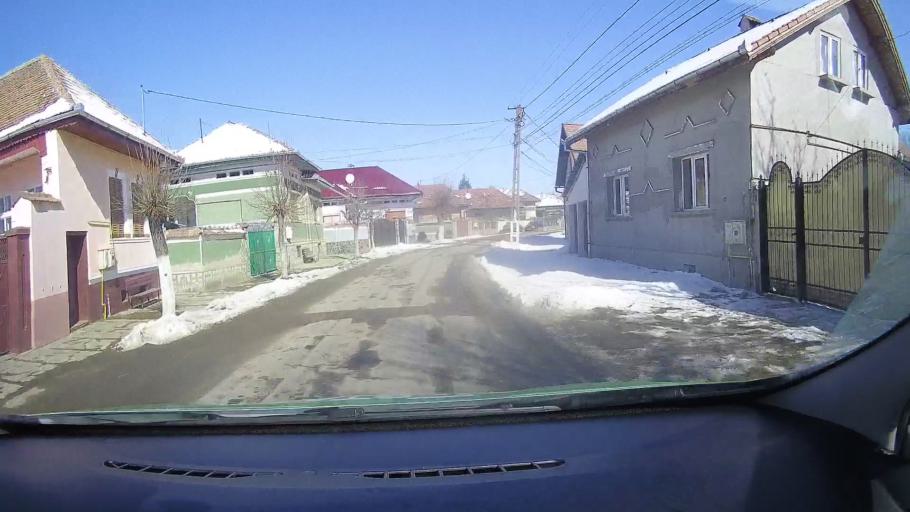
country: RO
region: Brasov
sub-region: Comuna Mandra
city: Mandra
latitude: 45.8223
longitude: 25.0062
